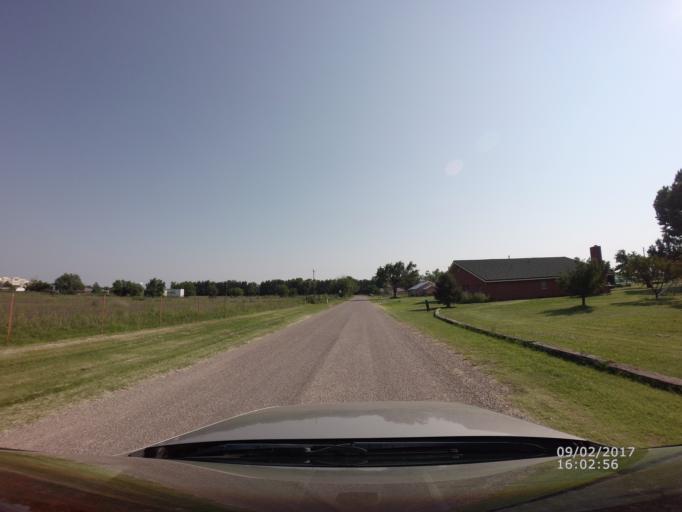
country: US
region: New Mexico
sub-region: Curry County
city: Clovis
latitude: 34.4430
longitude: -103.1996
